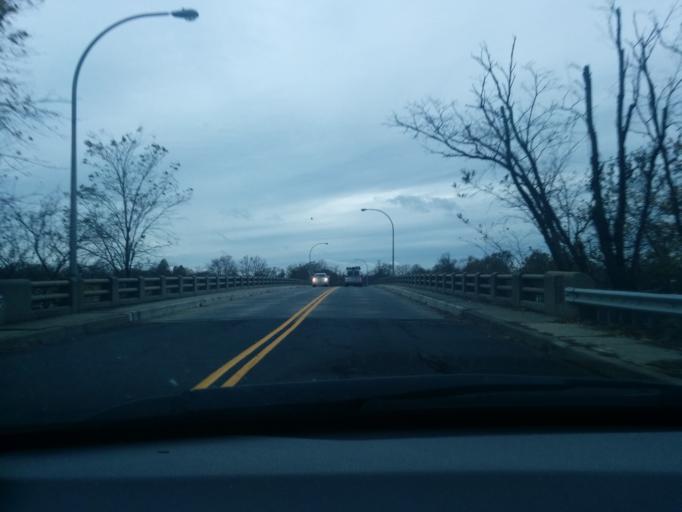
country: US
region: New Jersey
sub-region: Monmouth County
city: Long Branch
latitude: 40.3202
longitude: -73.9949
